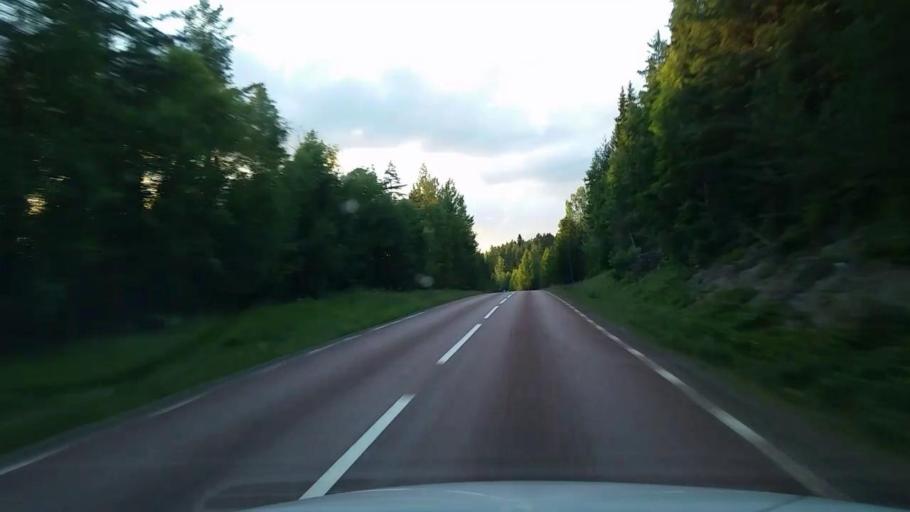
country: SE
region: Vaesternorrland
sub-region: Ange Kommun
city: Ange
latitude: 62.1497
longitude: 15.6829
